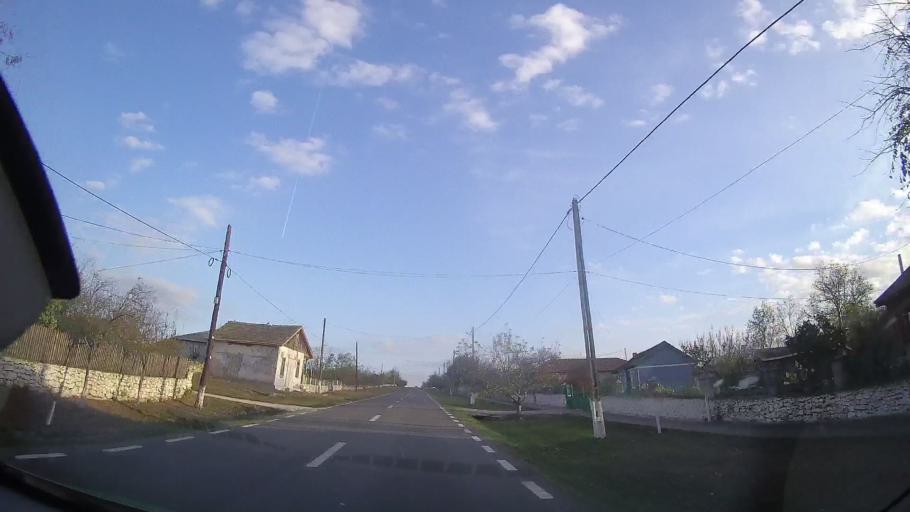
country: RO
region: Constanta
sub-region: Comuna Chirnogeni
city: Plopeni
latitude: 43.9606
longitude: 28.1436
